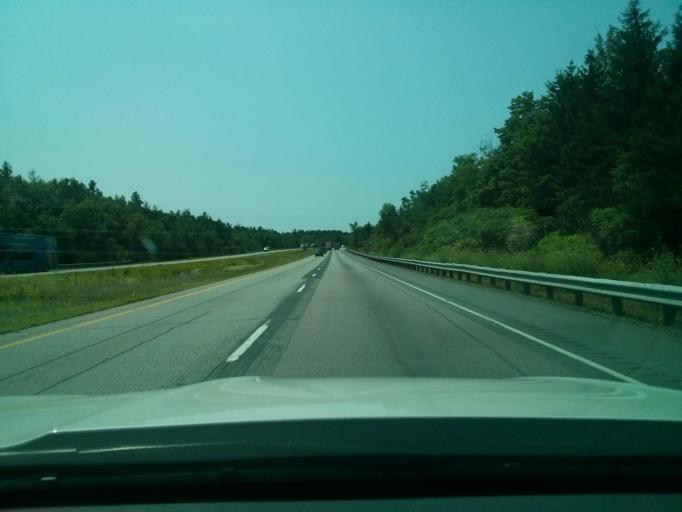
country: US
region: New York
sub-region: Jefferson County
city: Alexandria Bay
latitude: 44.4296
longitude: -75.8983
